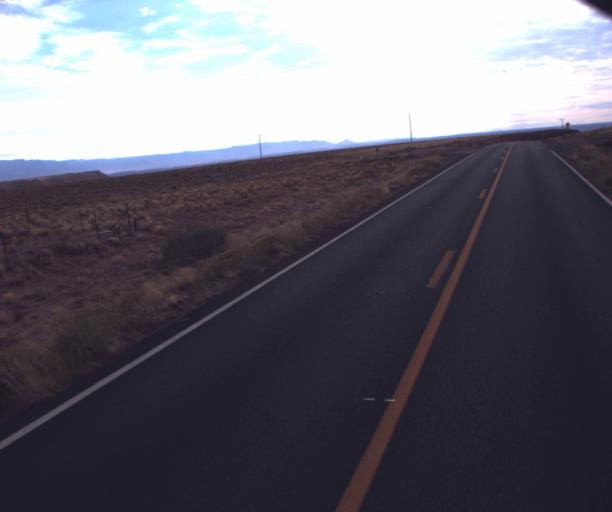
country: US
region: Arizona
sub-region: Apache County
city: Many Farms
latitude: 36.5525
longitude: -109.5326
